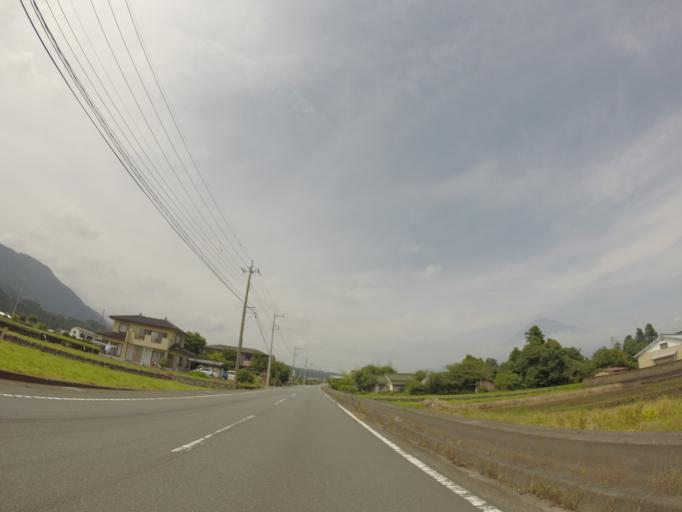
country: JP
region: Shizuoka
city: Fujinomiya
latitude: 35.2825
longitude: 138.5754
